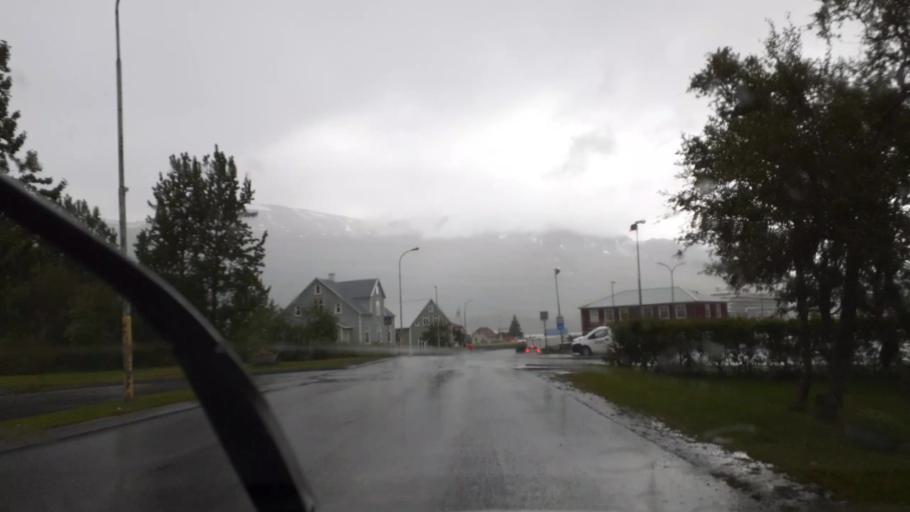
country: IS
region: East
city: Eskifjoerdur
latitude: 65.2596
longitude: -14.0102
